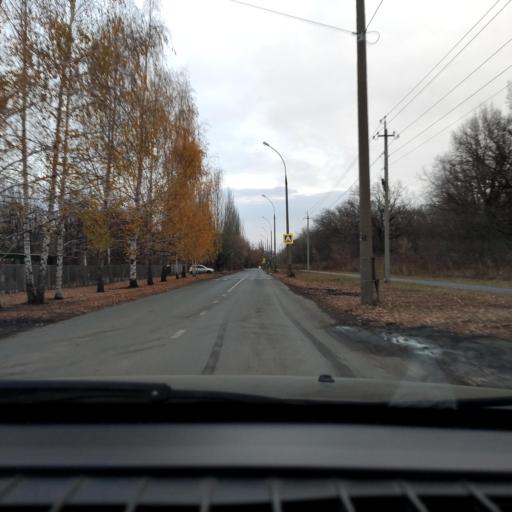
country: RU
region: Samara
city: Tol'yatti
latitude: 53.5099
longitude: 49.3082
